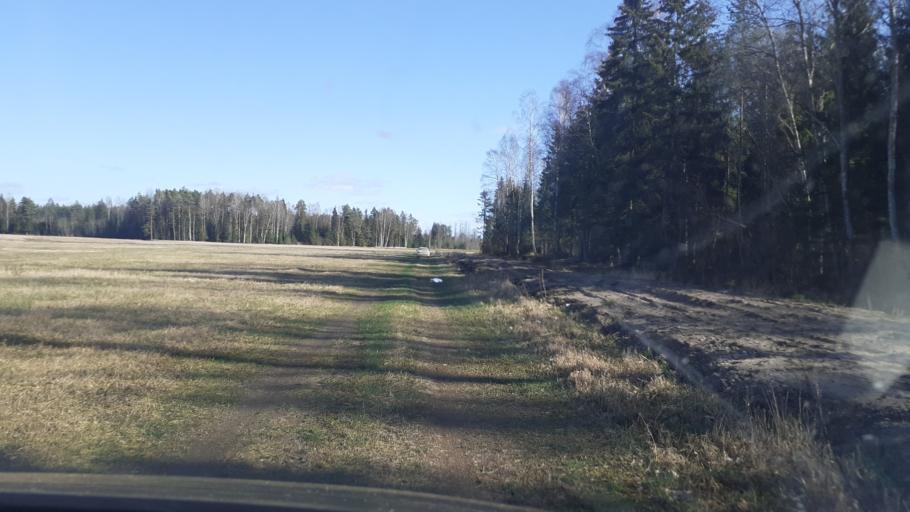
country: LV
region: Kuldigas Rajons
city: Kuldiga
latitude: 56.8759
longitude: 22.1105
